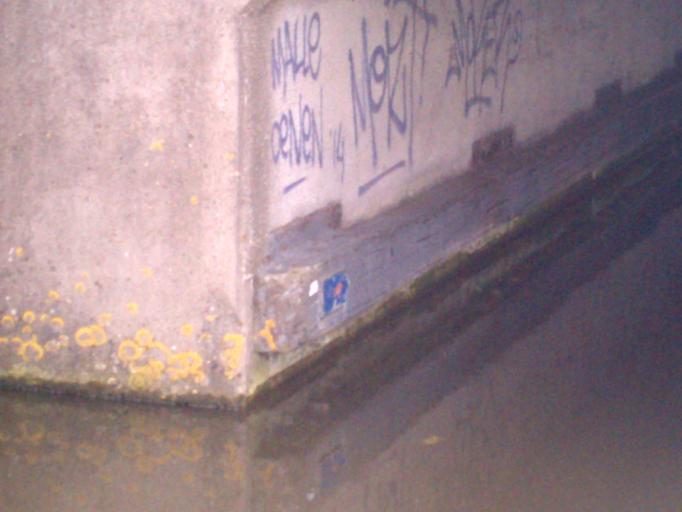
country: NL
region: South Holland
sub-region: Gemeente Teylingen
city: Sassenheim
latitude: 52.2225
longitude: 4.5393
